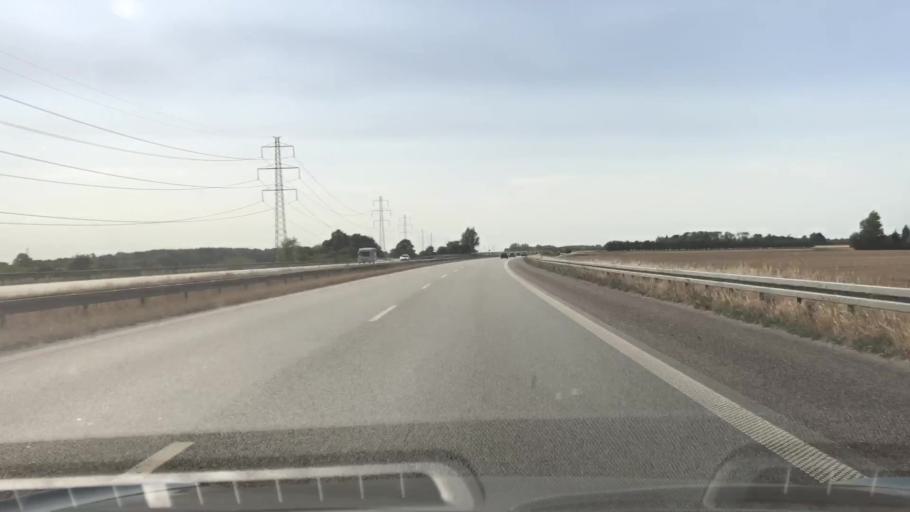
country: DK
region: Zealand
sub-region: Ringsted Kommune
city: Ringsted
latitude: 55.4525
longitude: 11.8611
